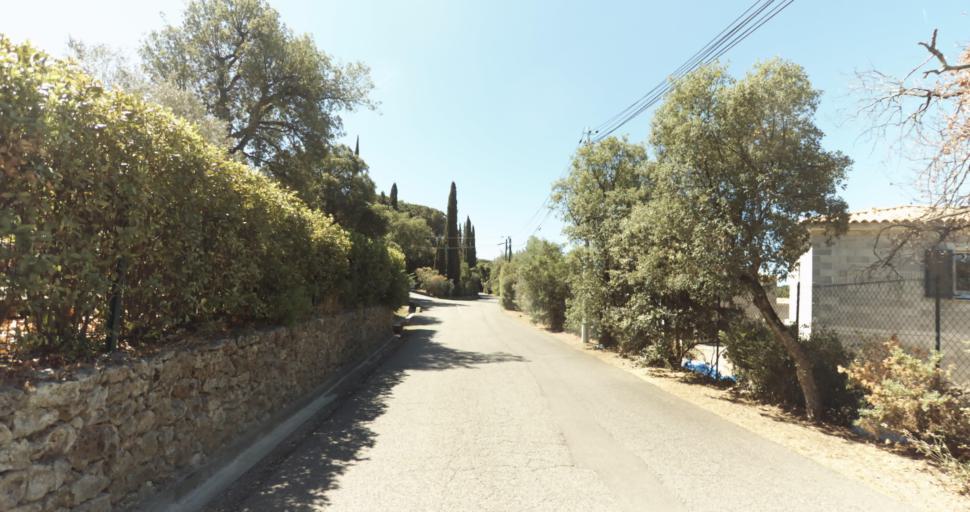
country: FR
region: Provence-Alpes-Cote d'Azur
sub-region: Departement du Var
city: Gassin
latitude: 43.2598
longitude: 6.6000
